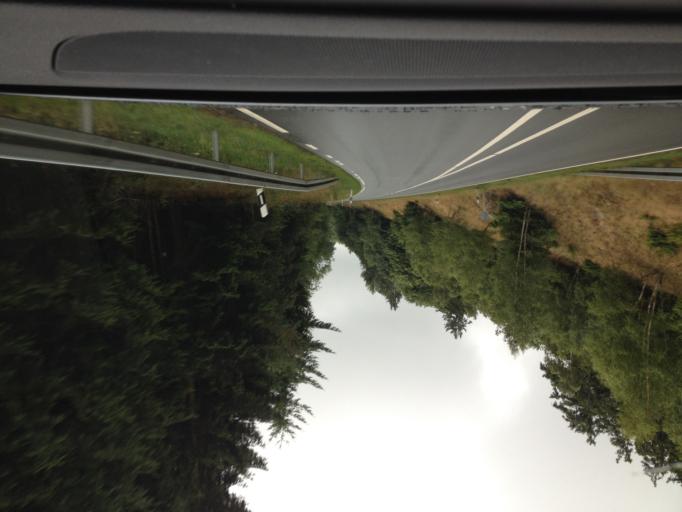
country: DE
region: Hesse
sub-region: Regierungsbezirk Darmstadt
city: Schlangenbad
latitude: 50.1138
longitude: 8.1198
